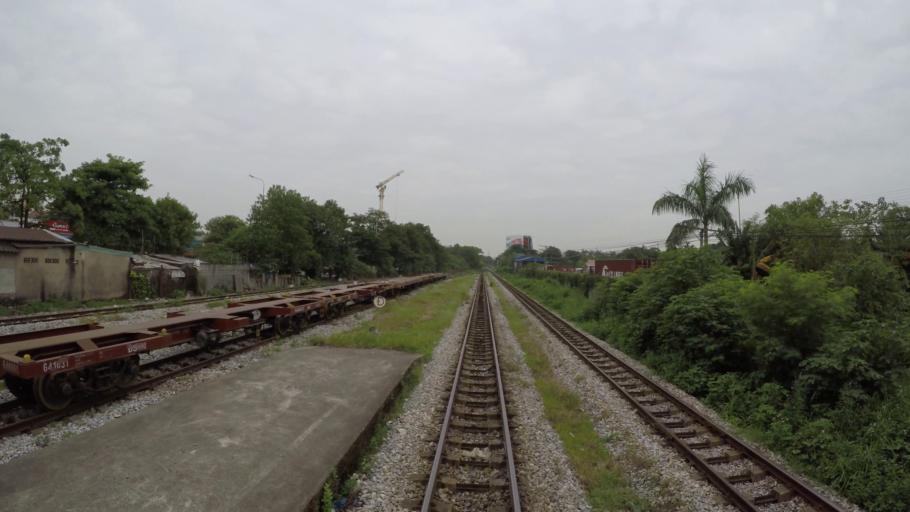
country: VN
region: Hai Phong
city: An Duong
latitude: 20.8795
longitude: 106.6243
